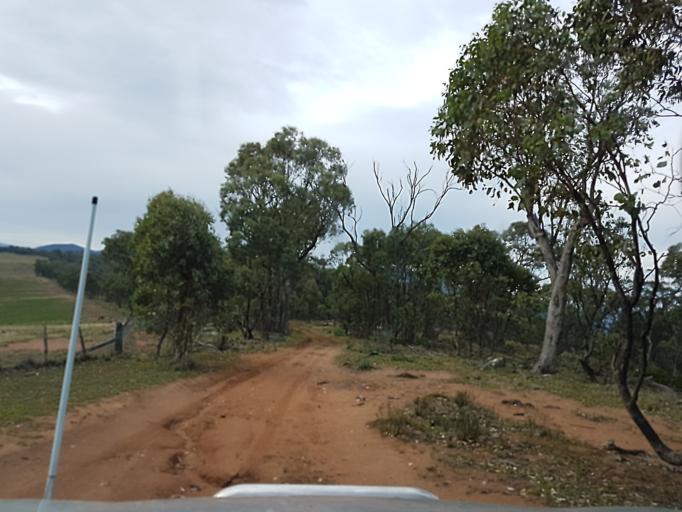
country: AU
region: New South Wales
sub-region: Snowy River
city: Jindabyne
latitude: -36.9657
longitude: 148.3842
